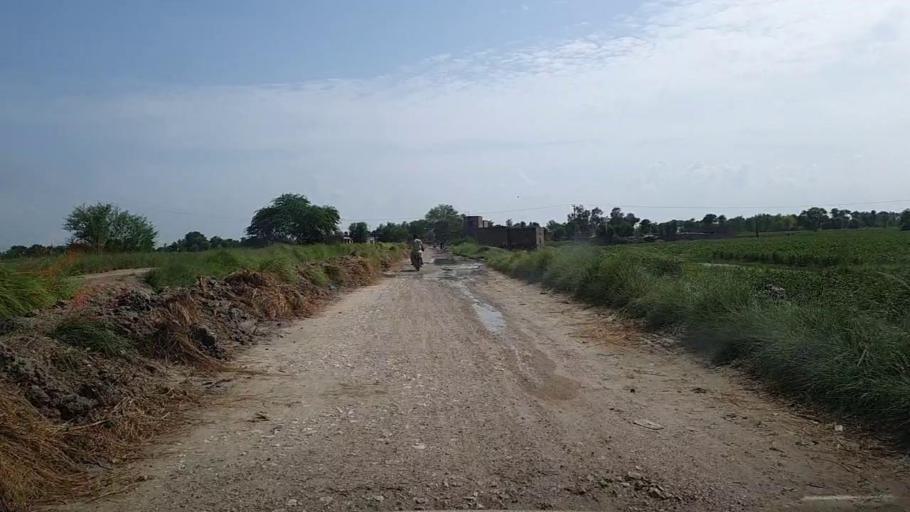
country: PK
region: Sindh
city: Bhiria
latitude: 26.8800
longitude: 68.2316
